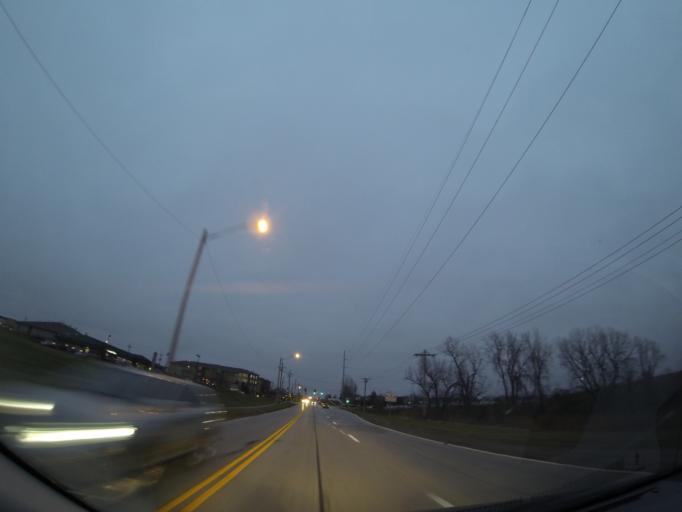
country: US
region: Nebraska
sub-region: Douglas County
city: Elkhorn
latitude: 41.2762
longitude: -96.1772
